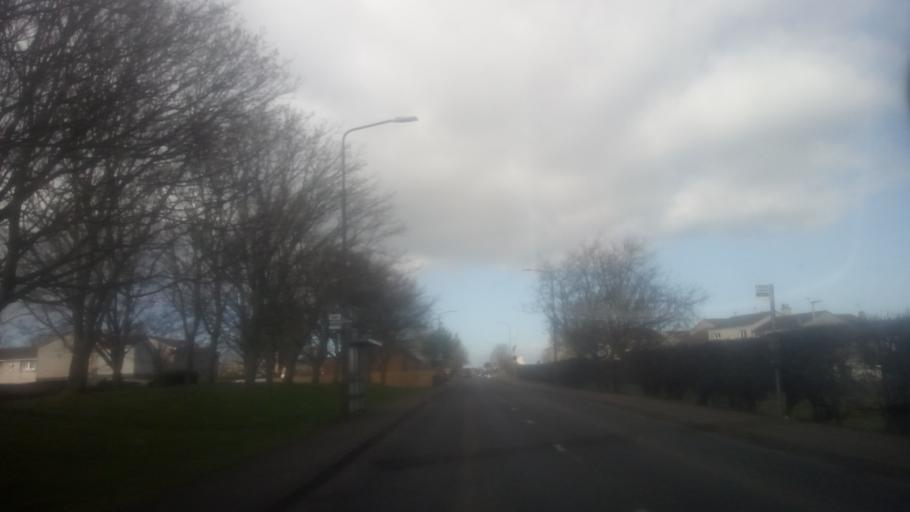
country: GB
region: Scotland
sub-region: East Lothian
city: Tranent
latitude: 55.9378
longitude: -2.9433
